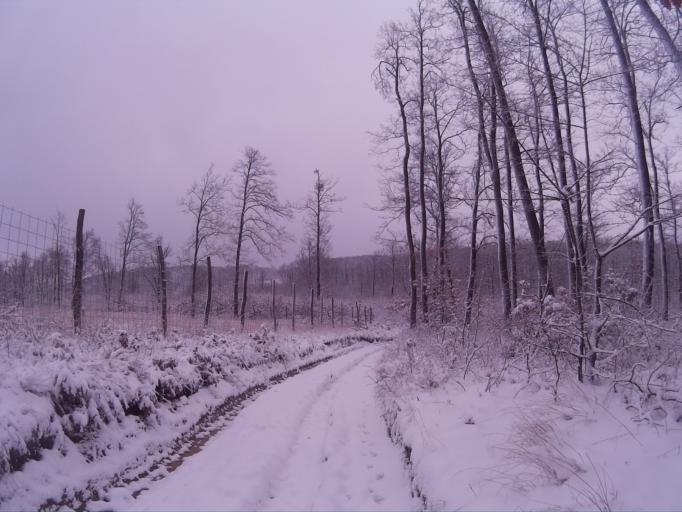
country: HU
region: Komarom-Esztergom
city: Tarjan
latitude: 47.5636
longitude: 18.5336
